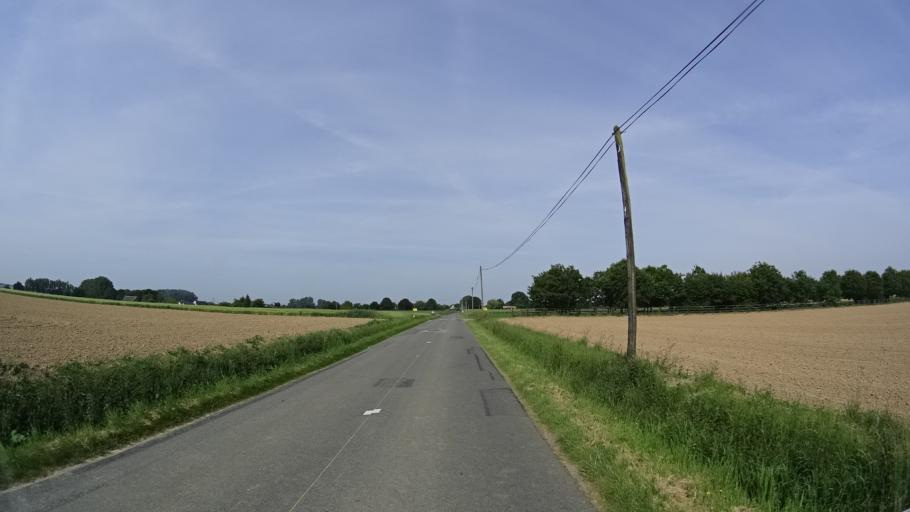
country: FR
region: Brittany
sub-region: Departement d'Ille-et-Vilaine
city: Chateaugiron
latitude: 48.0333
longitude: -1.5083
